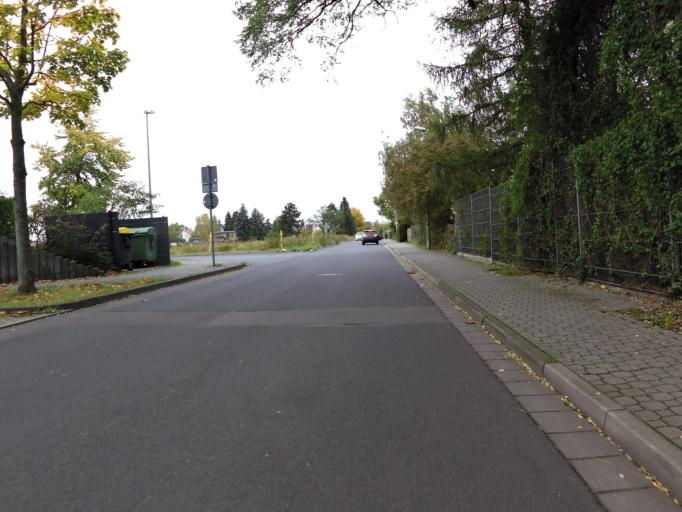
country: DE
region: Saxony
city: Grossposna
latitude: 51.3030
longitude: 12.4418
